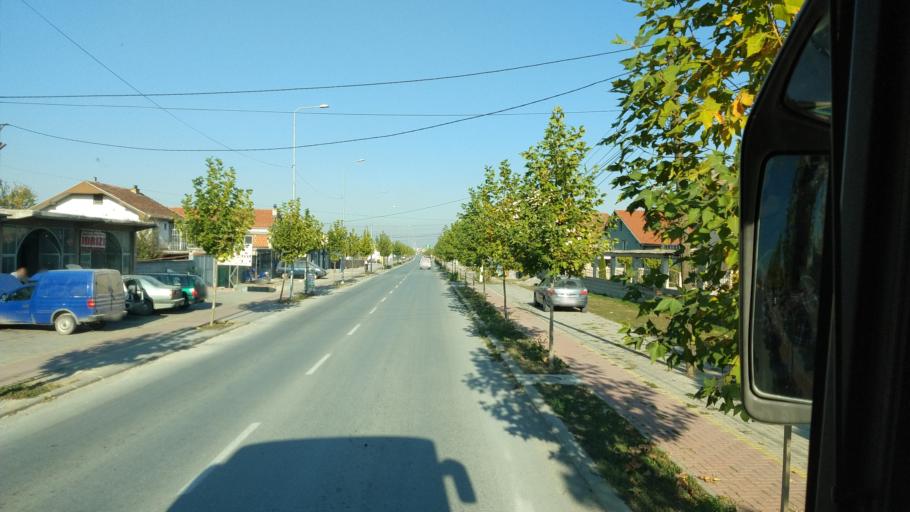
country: XK
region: Ferizaj
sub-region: Komuna e Shtimes
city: Shtime
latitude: 42.4372
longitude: 21.0471
